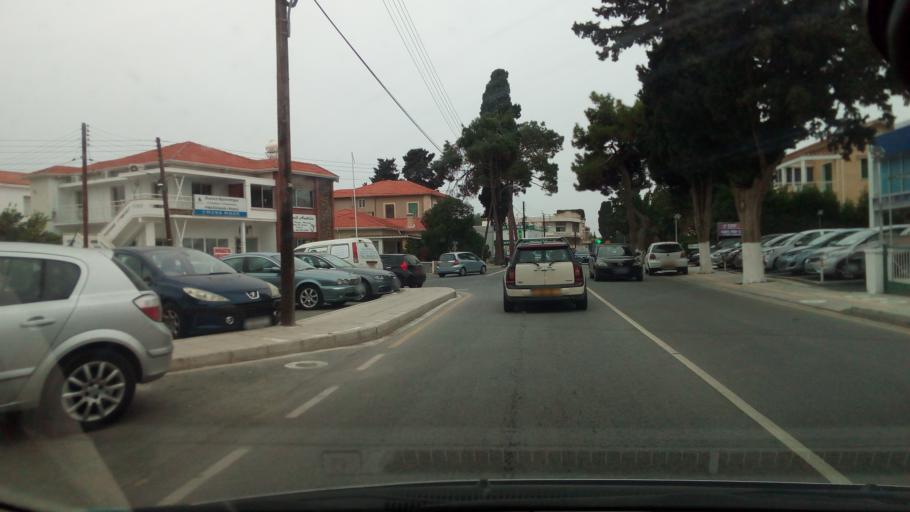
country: CY
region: Pafos
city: Paphos
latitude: 34.7724
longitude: 32.4271
